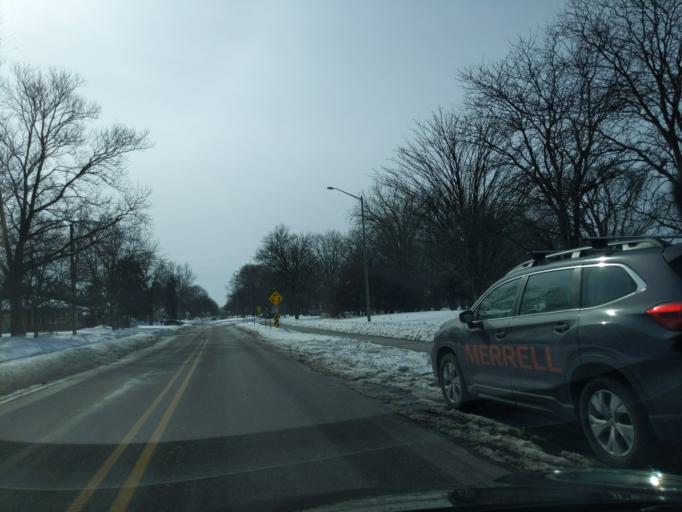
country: US
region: Michigan
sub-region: Kent County
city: Comstock Park
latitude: 43.0076
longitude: -85.6679
